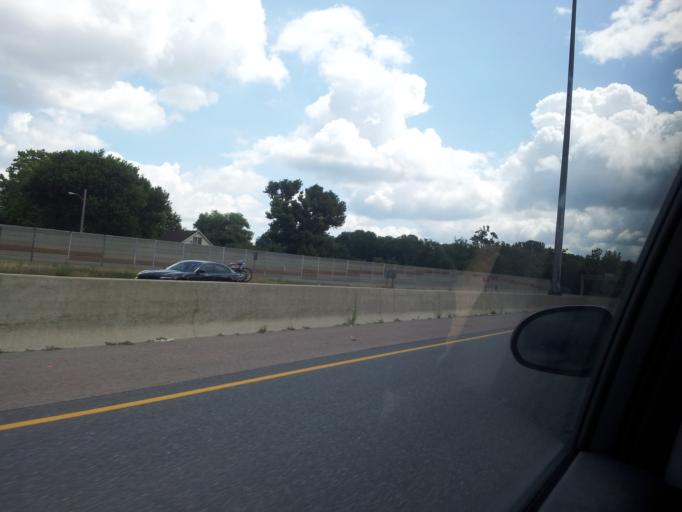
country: CA
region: Ontario
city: Kitchener
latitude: 43.4454
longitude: -80.4591
